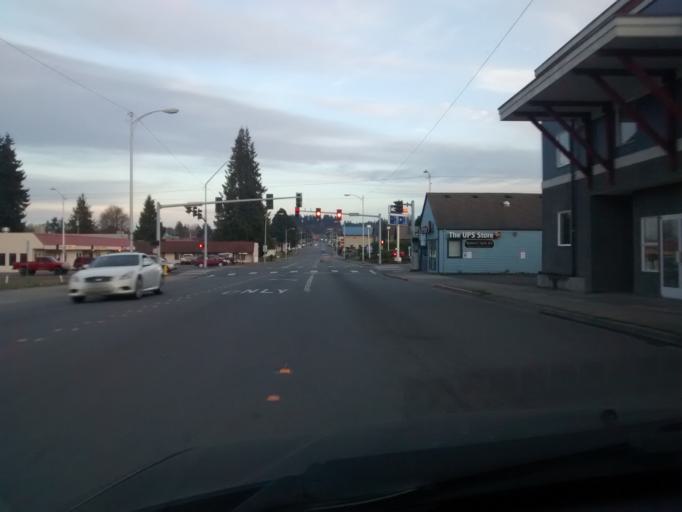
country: US
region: Washington
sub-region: Clallam County
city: Port Angeles
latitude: 48.1125
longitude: -123.4381
